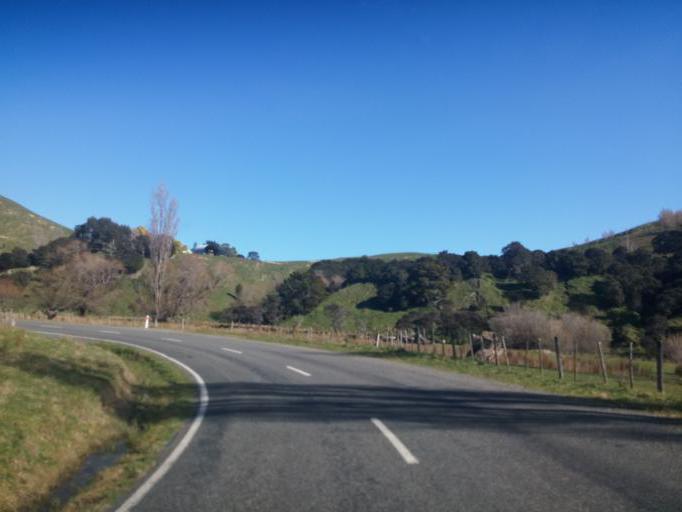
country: NZ
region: Wellington
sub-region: South Wairarapa District
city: Waipawa
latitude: -41.3919
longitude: 175.5065
